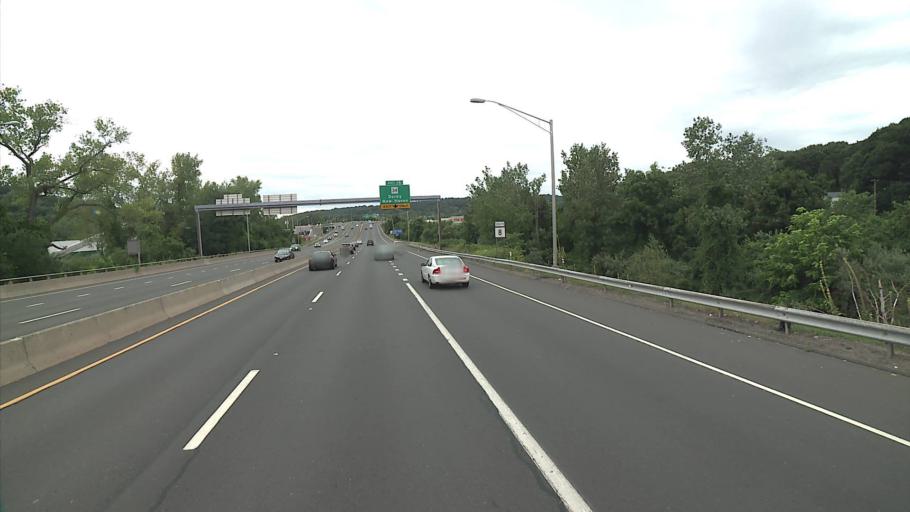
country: US
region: Connecticut
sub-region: New Haven County
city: Derby
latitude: 41.3242
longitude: -73.0851
